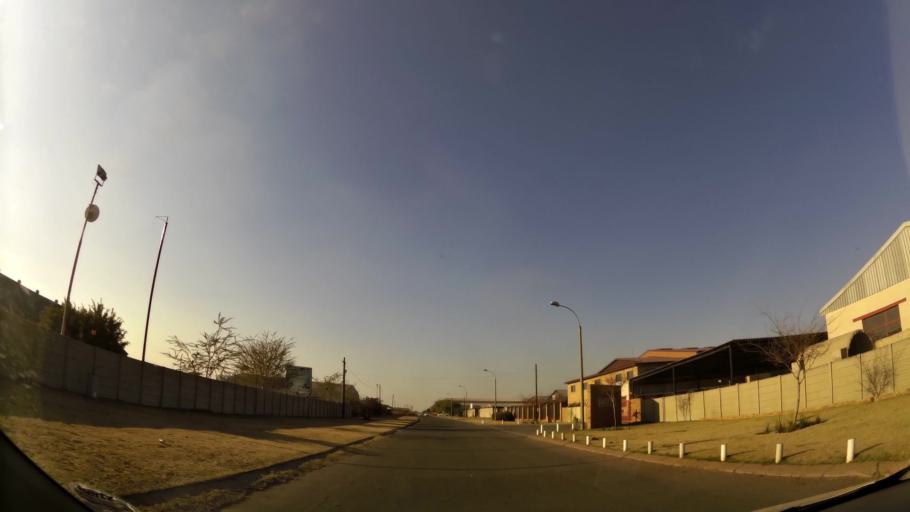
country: ZA
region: Gauteng
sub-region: West Rand District Municipality
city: Randfontein
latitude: -26.1982
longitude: 27.6901
